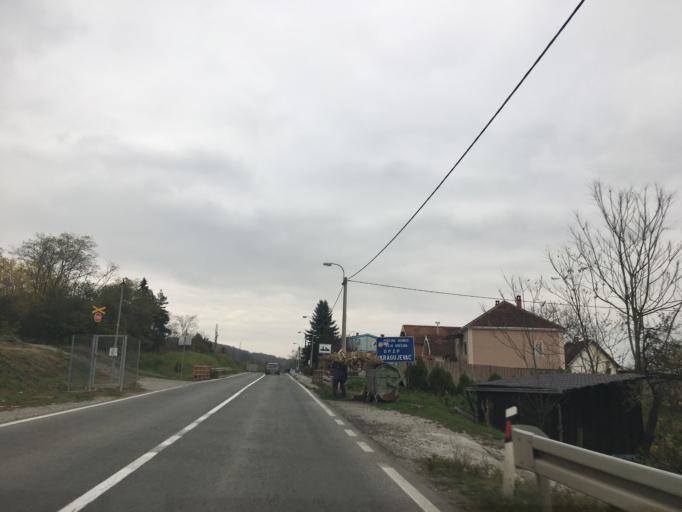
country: RS
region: Central Serbia
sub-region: Raski Okrug
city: Kraljevo
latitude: 43.7280
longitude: 20.7542
